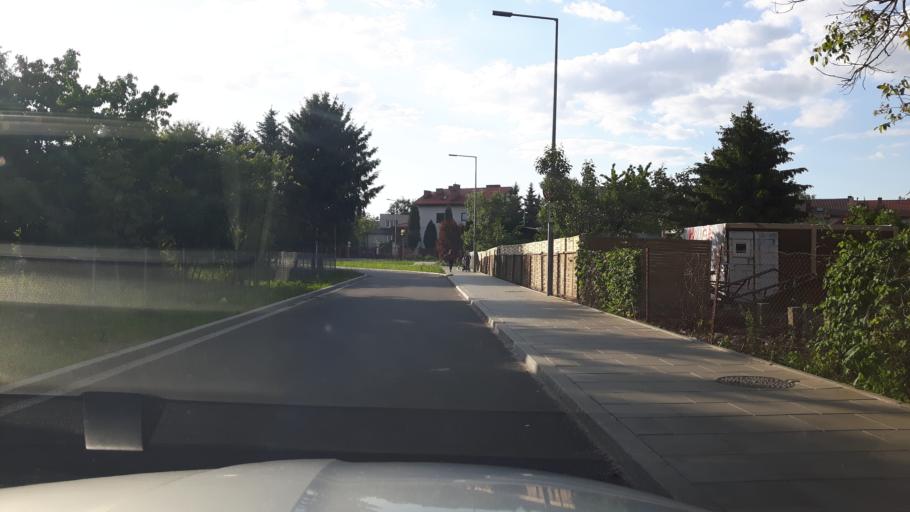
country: PL
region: Masovian Voivodeship
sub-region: Powiat wolominski
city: Zabki
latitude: 52.2784
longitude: 21.0796
